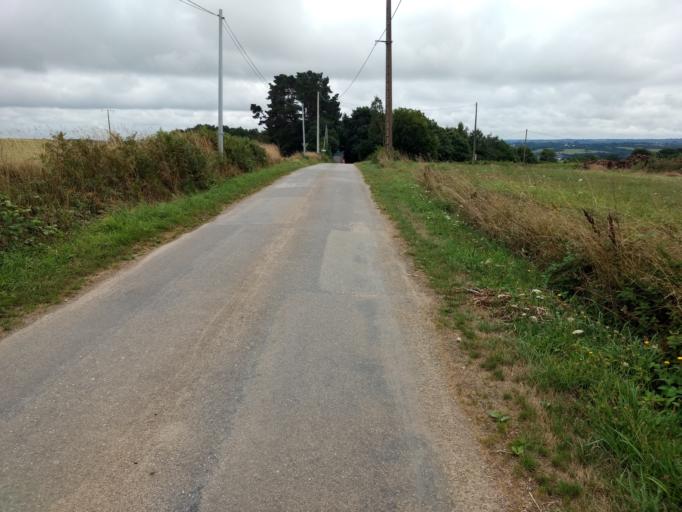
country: FR
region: Brittany
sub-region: Departement du Finistere
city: Loperhet
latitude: 48.3642
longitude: -4.2895
